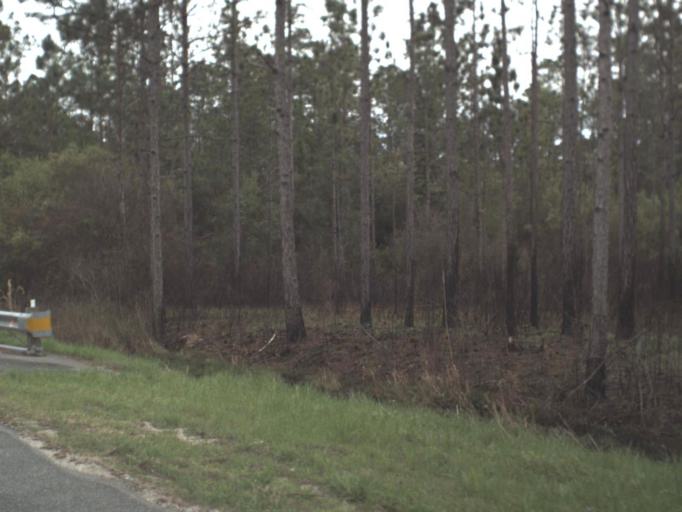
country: US
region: Florida
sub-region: Gadsden County
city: Midway
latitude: 30.3428
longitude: -84.4963
